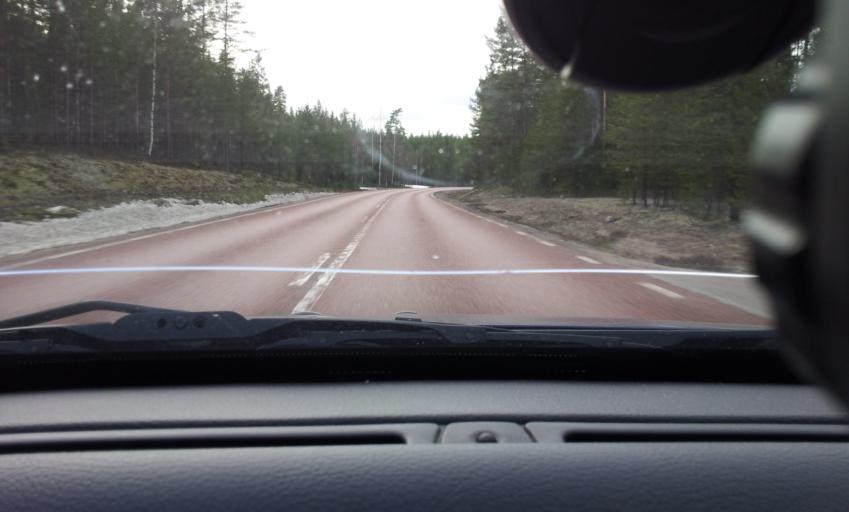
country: SE
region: Gaevleborg
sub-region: Ljusdals Kommun
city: Farila
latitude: 61.9001
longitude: 15.6460
